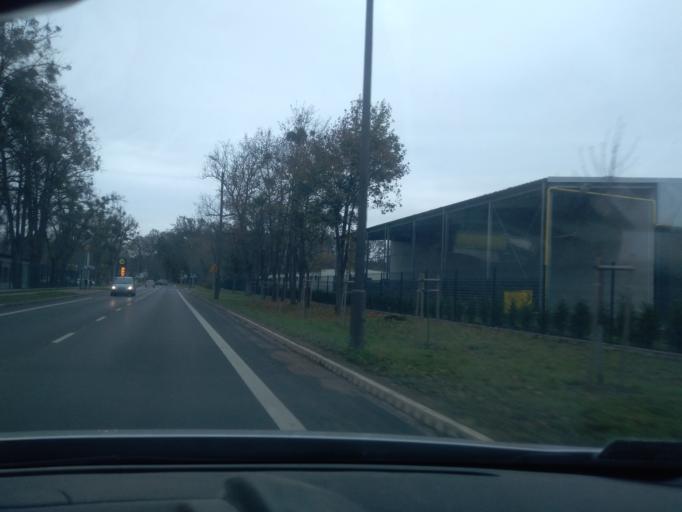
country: PL
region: Greater Poland Voivodeship
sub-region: Powiat poznanski
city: Murowana Goslina
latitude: 52.5369
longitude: 16.9438
